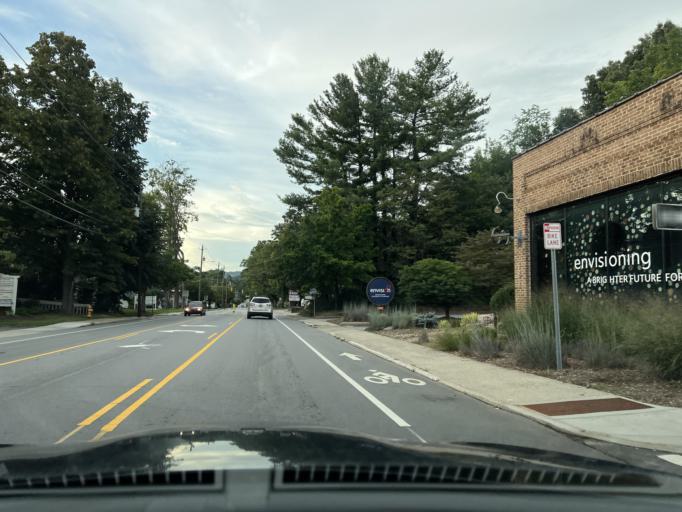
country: US
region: North Carolina
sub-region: Buncombe County
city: Asheville
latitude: 35.6056
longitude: -82.5464
